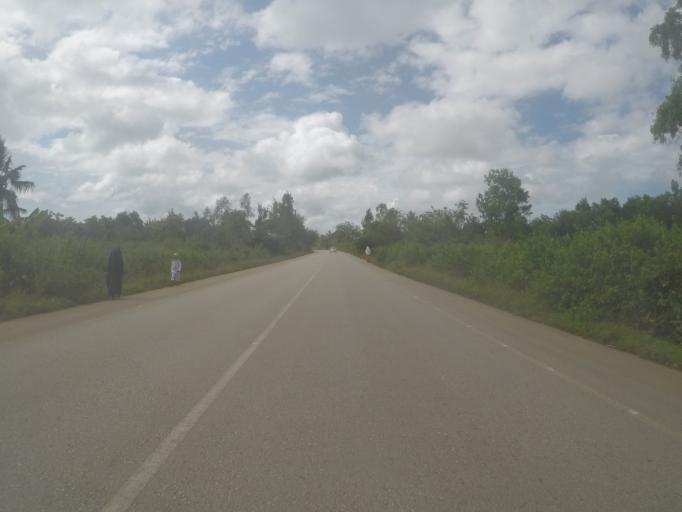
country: TZ
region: Zanzibar North
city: Kijini
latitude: -5.8507
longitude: 39.2831
